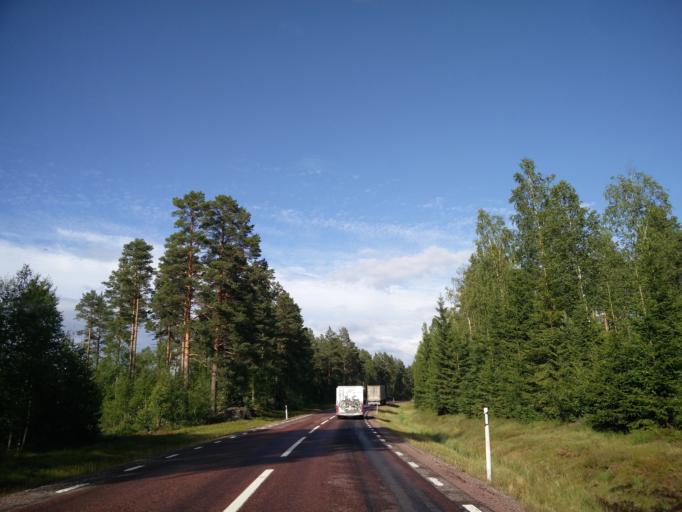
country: SE
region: Vaermland
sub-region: Hagfors Kommun
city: Ekshaerad
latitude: 60.4808
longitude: 13.3861
